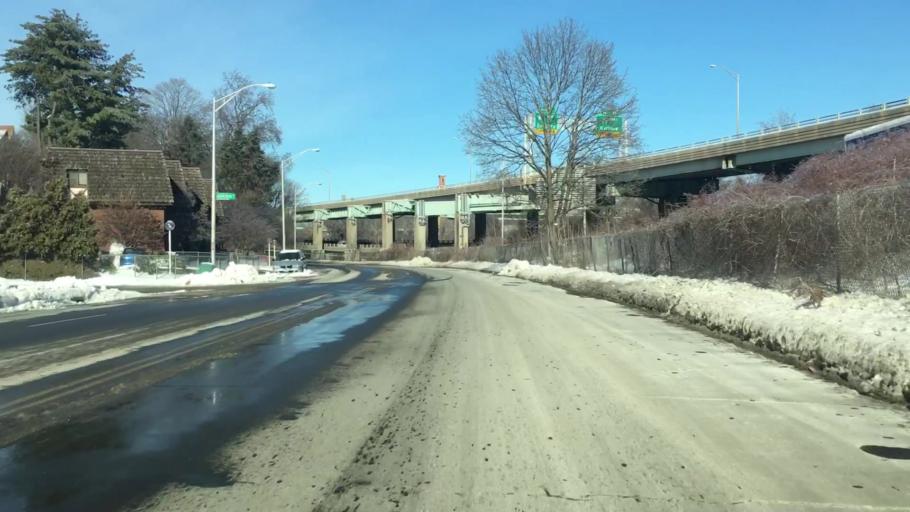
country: US
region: Connecticut
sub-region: New Haven County
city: Waterbury
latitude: 41.5467
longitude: -73.0451
